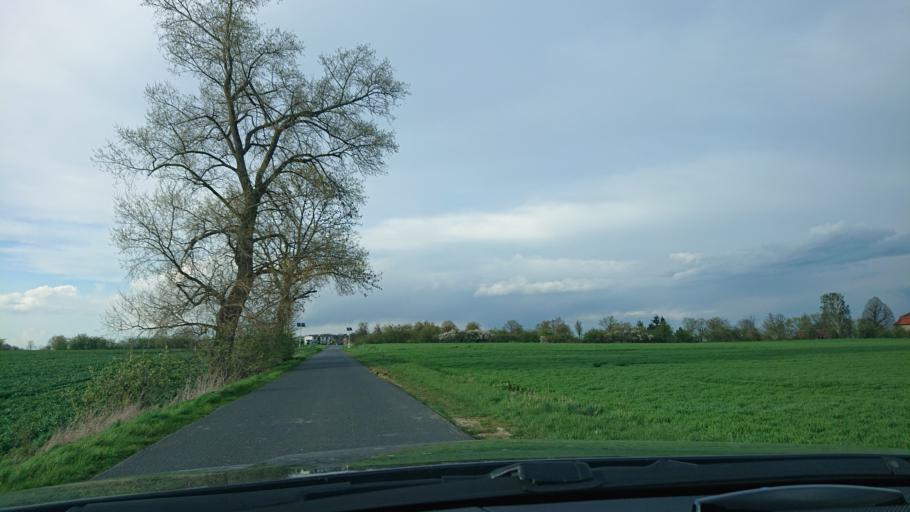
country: PL
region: Greater Poland Voivodeship
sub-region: Powiat gnieznienski
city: Klecko
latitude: 52.5847
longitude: 17.4839
